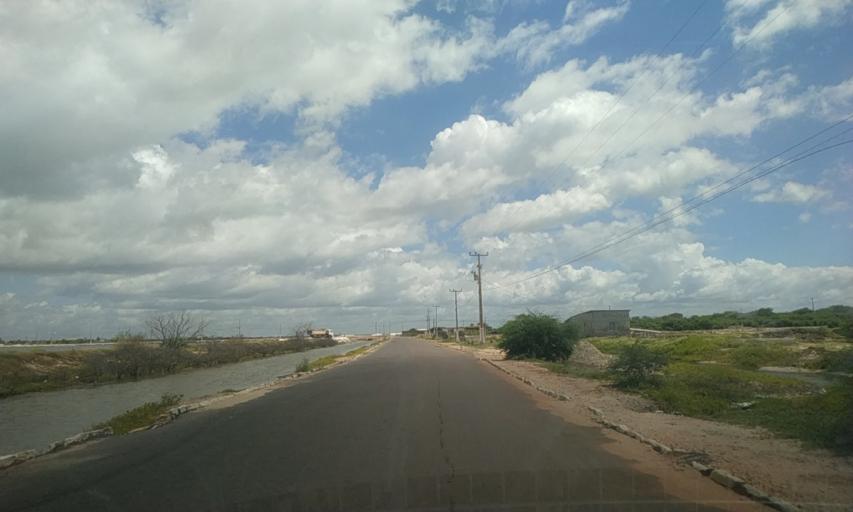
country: BR
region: Rio Grande do Norte
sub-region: Areia Branca
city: Areia Branca
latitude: -4.9343
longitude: -37.1116
